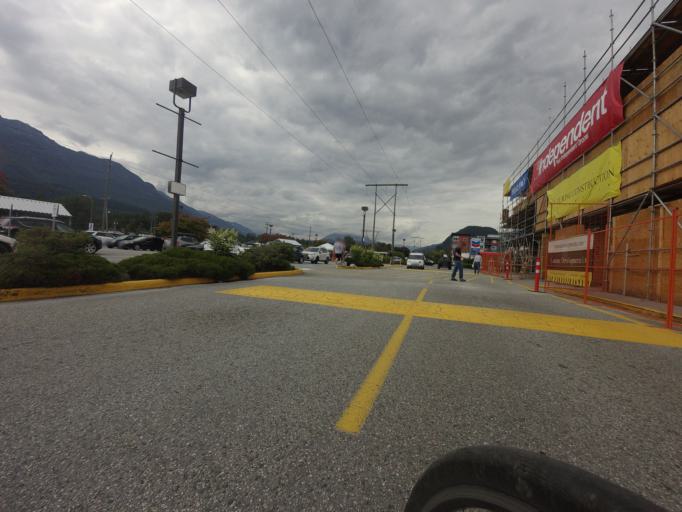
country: CA
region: British Columbia
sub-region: Greater Vancouver Regional District
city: Lions Bay
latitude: 49.7400
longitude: -123.1340
